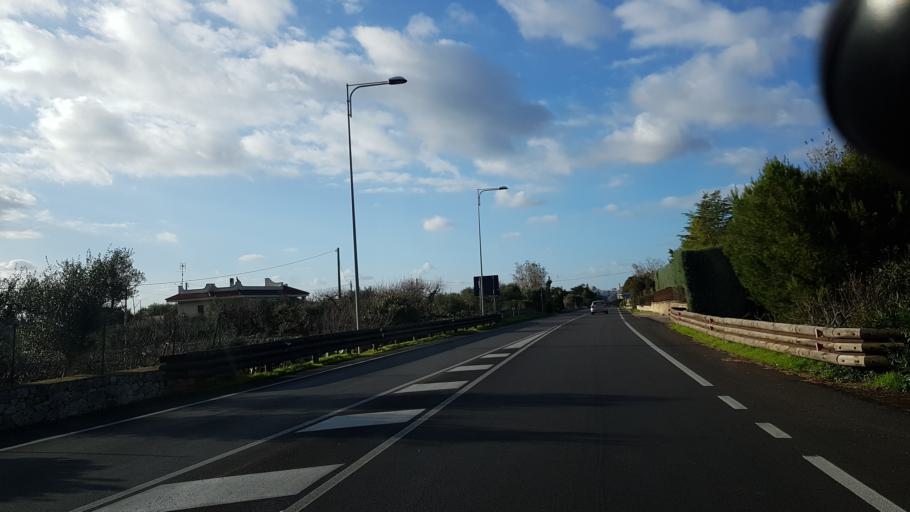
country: IT
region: Apulia
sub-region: Provincia di Bari
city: Putignano
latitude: 40.8407
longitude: 17.1477
